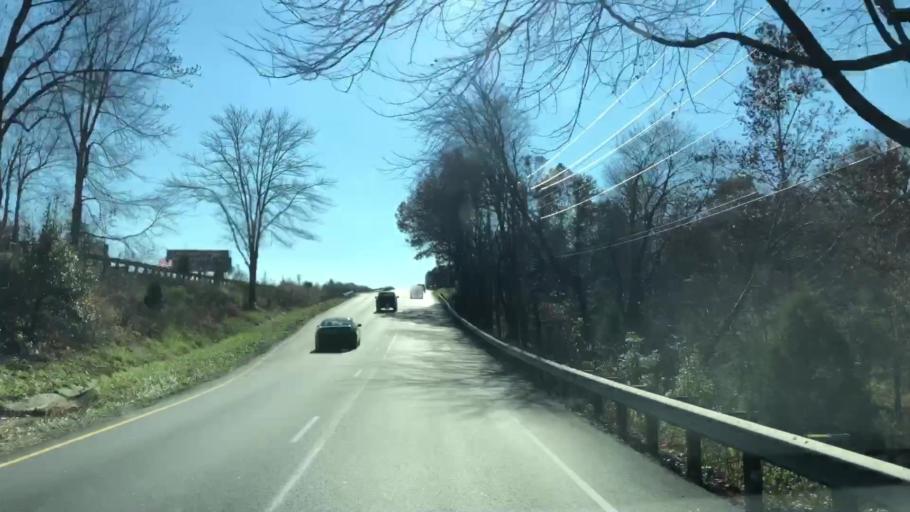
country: US
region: Virginia
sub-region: Greene County
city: Ruckersville
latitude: 38.1952
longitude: -78.3947
